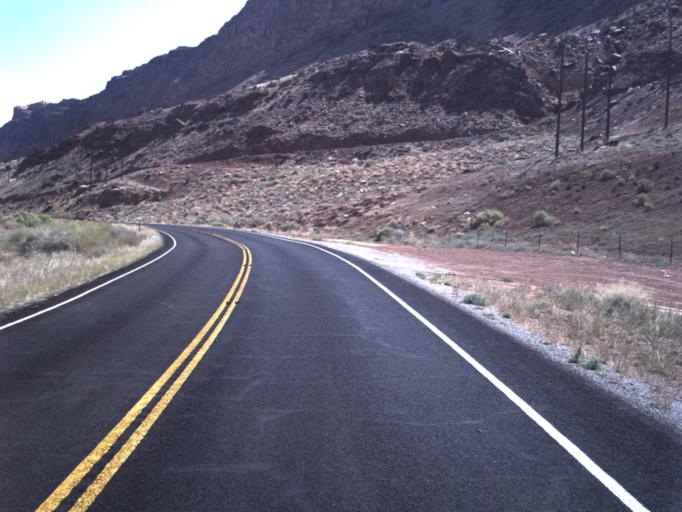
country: US
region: Utah
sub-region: Grand County
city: Moab
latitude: 38.6018
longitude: -109.6039
